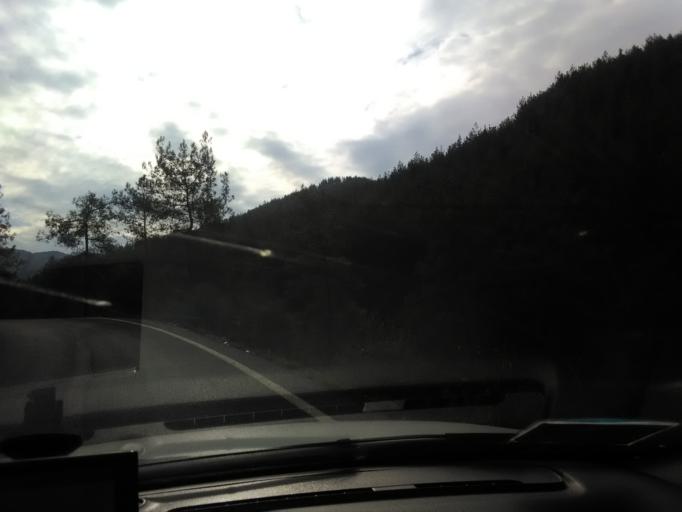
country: TR
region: Antalya
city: Gazipasa
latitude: 36.2451
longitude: 32.4140
